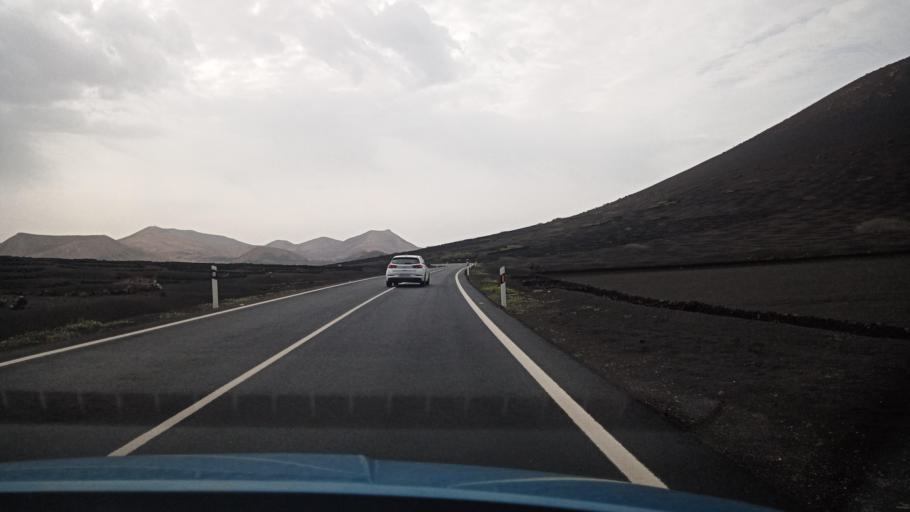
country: ES
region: Canary Islands
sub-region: Provincia de Las Palmas
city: Yaiza
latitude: 28.9675
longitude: -13.7174
